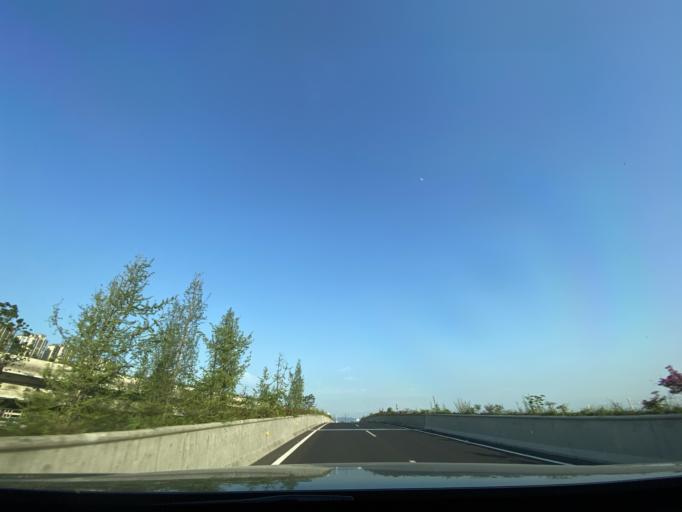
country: CN
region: Sichuan
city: Chengdu
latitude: 30.5980
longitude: 104.1162
